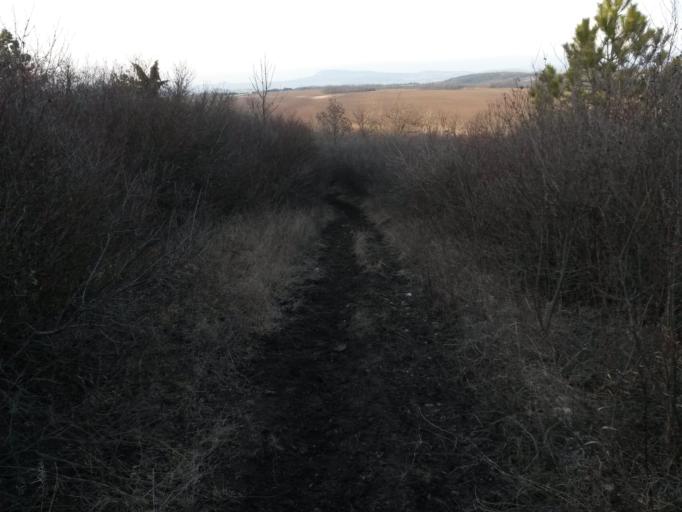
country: HU
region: Pest
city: Perbal
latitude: 47.5949
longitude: 18.7264
